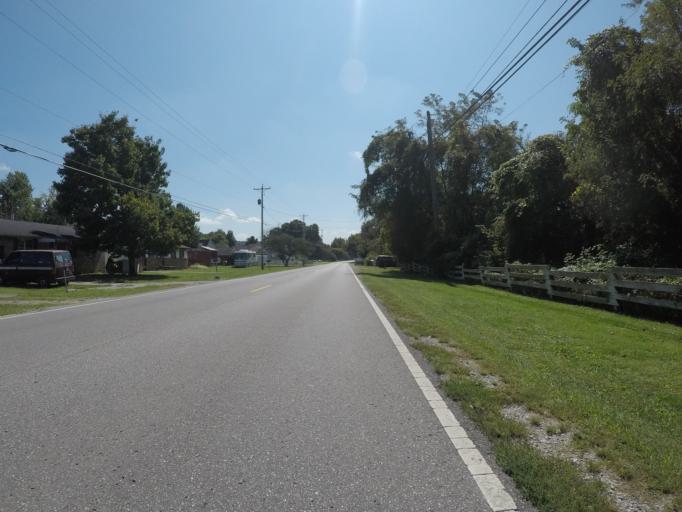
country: US
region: Kentucky
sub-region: Boyd County
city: Ashland
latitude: 38.4616
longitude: -82.5993
